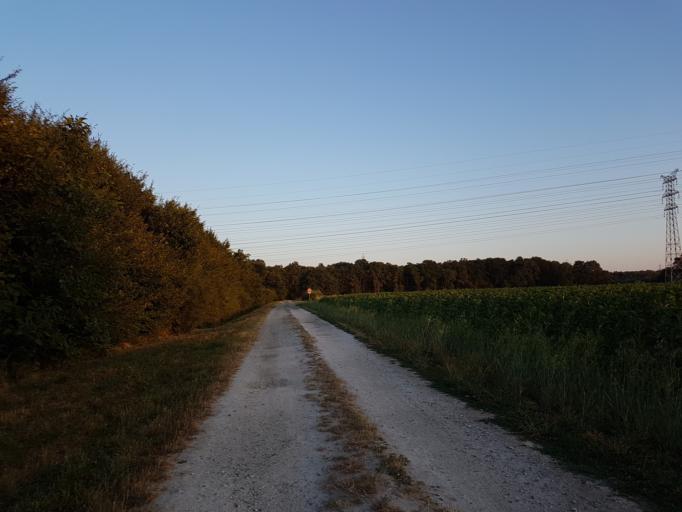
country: FR
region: Centre
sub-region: Departement d'Indre-et-Loire
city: Saint-Avertin
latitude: 47.3535
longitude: 0.7597
